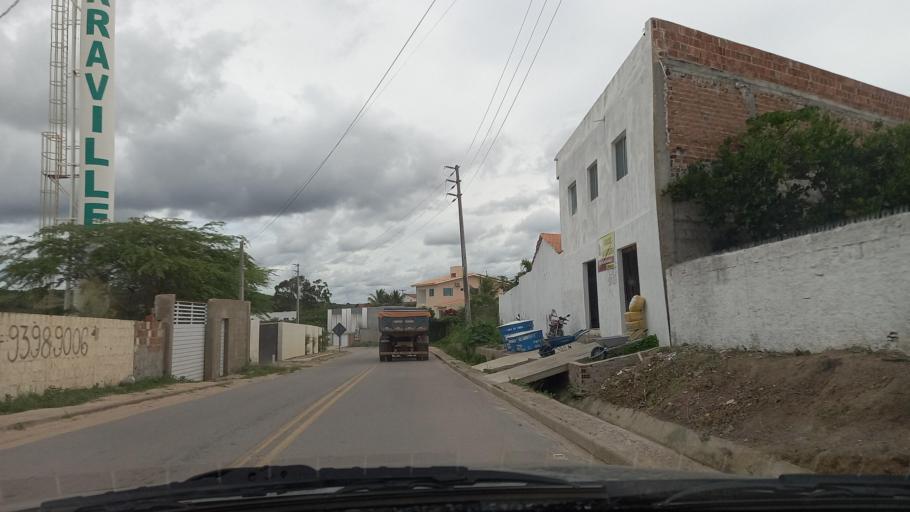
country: BR
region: Pernambuco
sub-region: Gravata
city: Gravata
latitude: -8.2220
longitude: -35.5772
